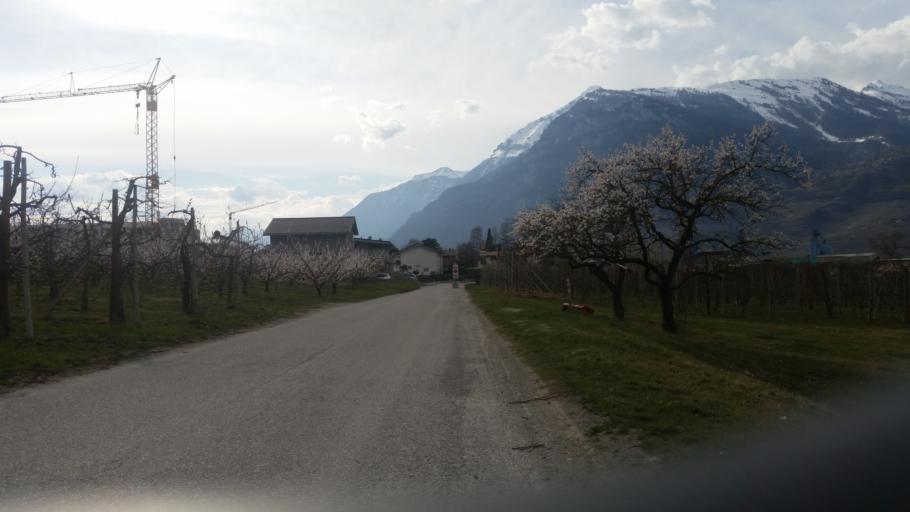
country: CH
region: Valais
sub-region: Martigny District
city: Riddes
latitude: 46.1756
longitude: 7.2319
